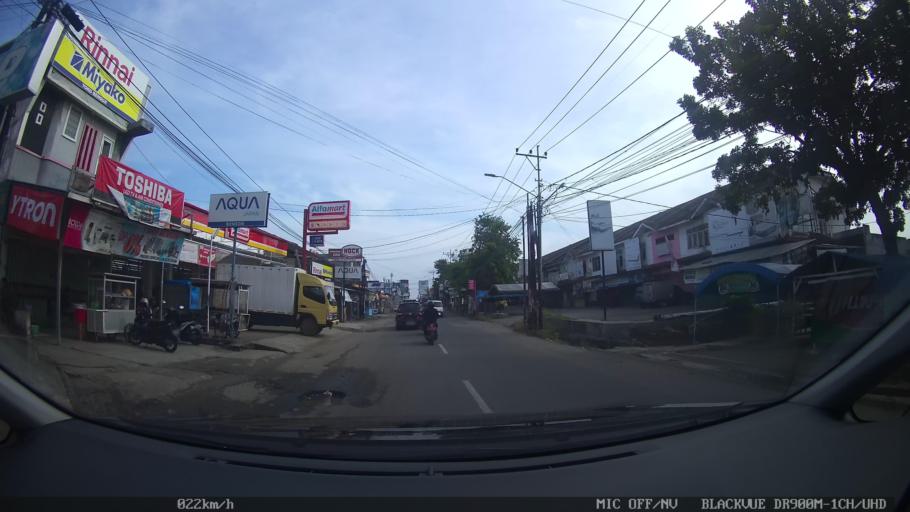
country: ID
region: Lampung
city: Kedaton
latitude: -5.3828
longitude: 105.2717
